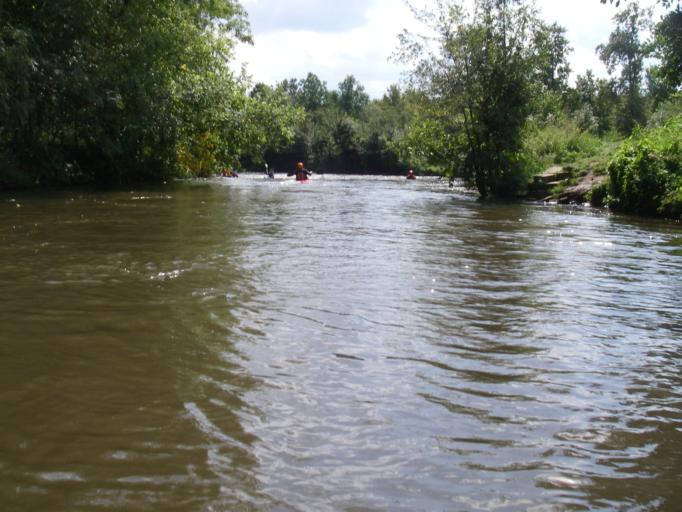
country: DE
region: North Rhine-Westphalia
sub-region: Regierungsbezirk Dusseldorf
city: Neuss
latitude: 51.1746
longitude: 6.7196
